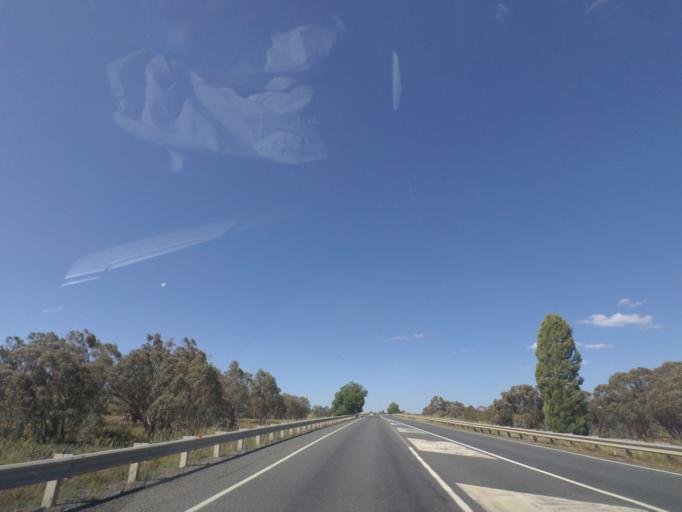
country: AU
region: New South Wales
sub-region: Albury Municipality
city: Lavington
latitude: -36.0037
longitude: 146.9873
